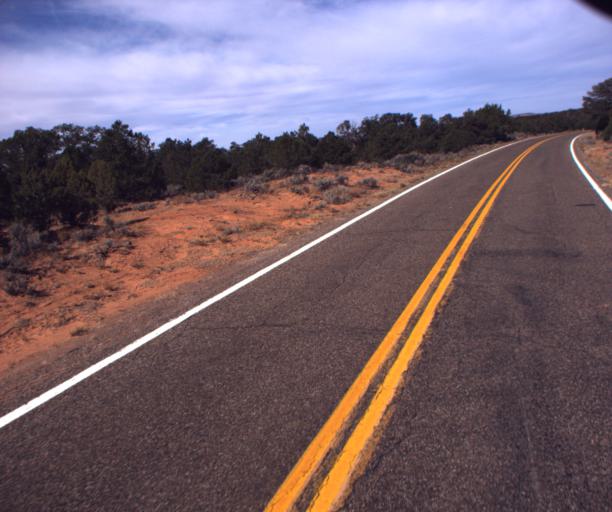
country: US
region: Arizona
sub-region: Navajo County
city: Kayenta
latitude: 36.5887
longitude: -110.4939
